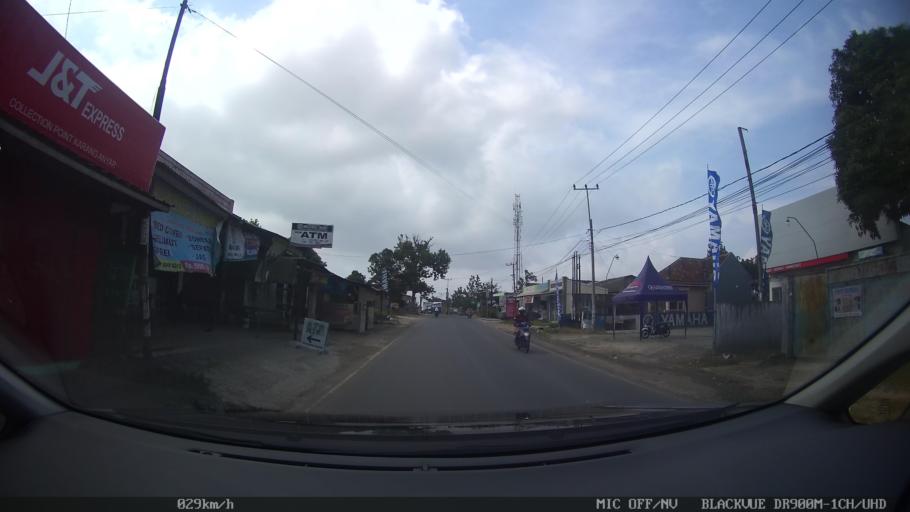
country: ID
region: Lampung
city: Kedaton
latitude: -5.3243
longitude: 105.2897
